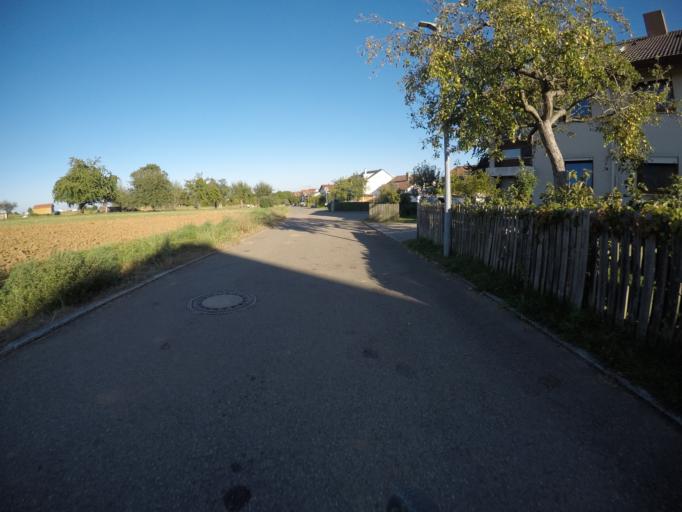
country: DE
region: Baden-Wuerttemberg
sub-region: Regierungsbezirk Stuttgart
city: Weil im Schonbuch
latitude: 48.6226
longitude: 9.0463
